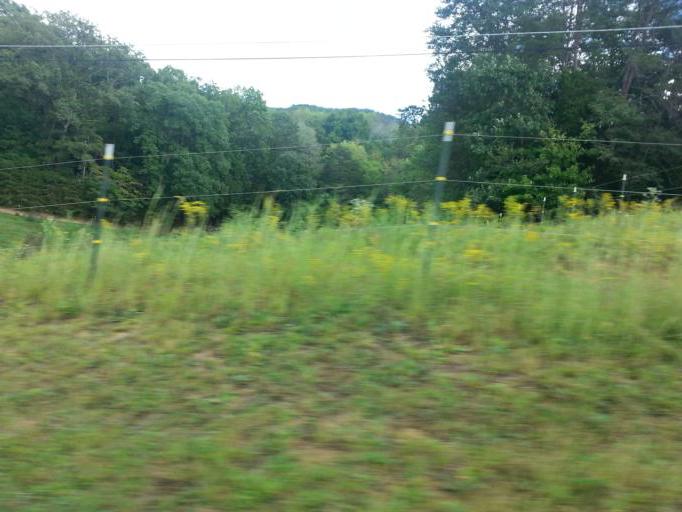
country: US
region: Tennessee
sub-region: Knox County
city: Mascot
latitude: 36.1131
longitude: -83.7809
